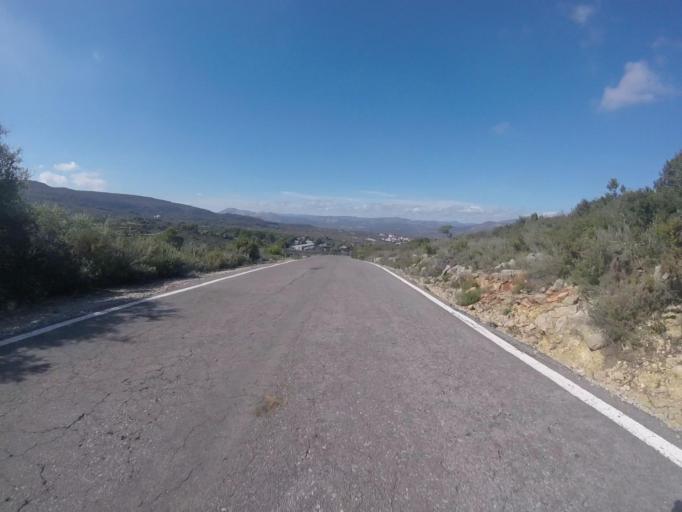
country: ES
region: Valencia
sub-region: Provincia de Castello
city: Albocasser
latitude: 40.3532
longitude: 0.0449
